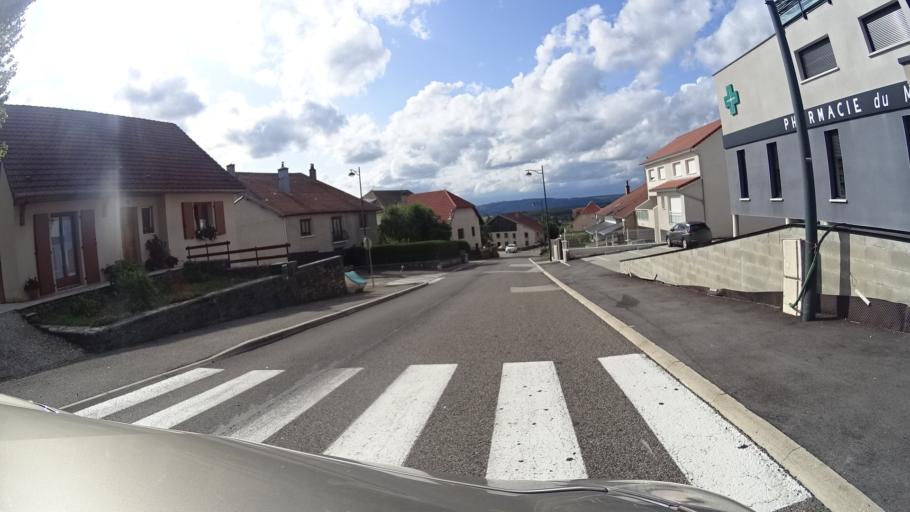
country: FR
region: Franche-Comte
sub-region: Departement du Doubs
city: Mamirolle
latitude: 47.1980
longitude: 6.1628
